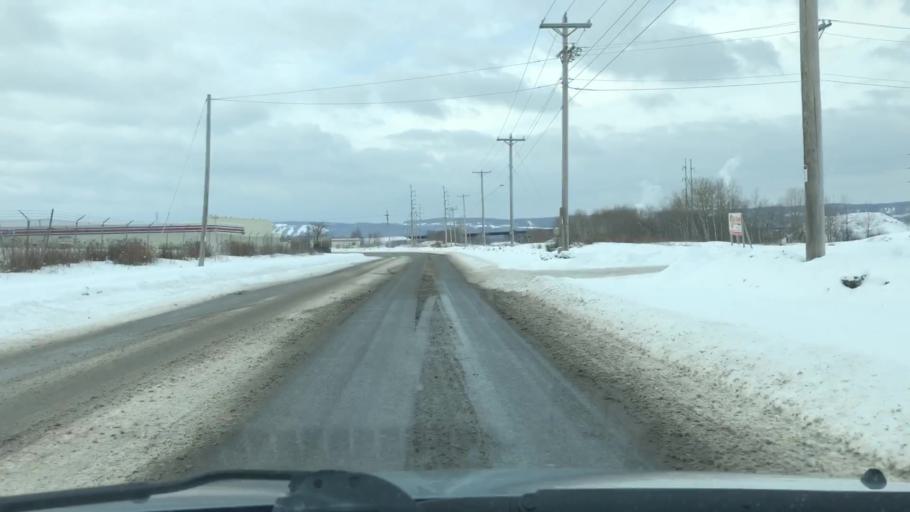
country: US
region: Wisconsin
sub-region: Douglas County
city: Superior
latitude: 46.7281
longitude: -92.1224
